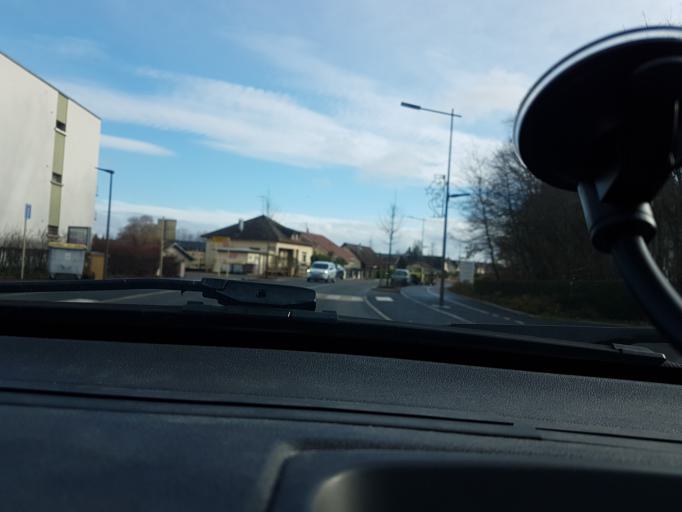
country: FR
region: Franche-Comte
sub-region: Territoire de Belfort
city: Bavilliers
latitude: 47.6222
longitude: 6.8456
